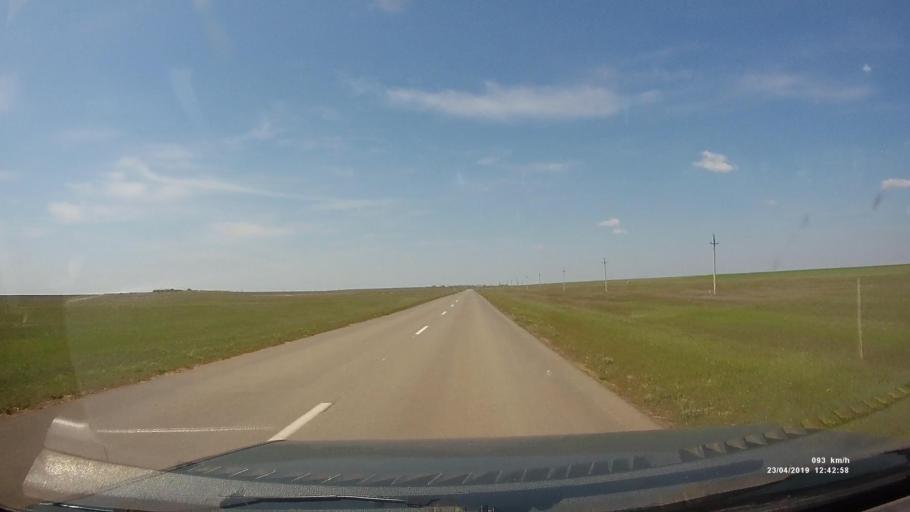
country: RU
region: Kalmykiya
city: Yashalta
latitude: 46.4602
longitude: 42.6572
